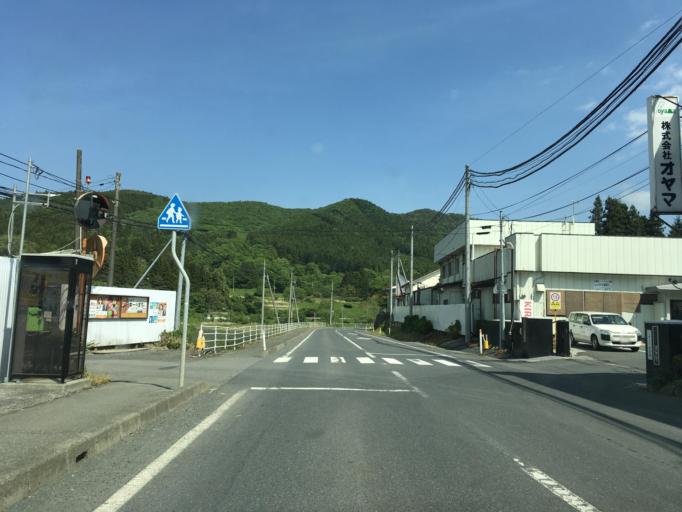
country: JP
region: Iwate
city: Ofunato
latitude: 38.9358
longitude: 141.4639
